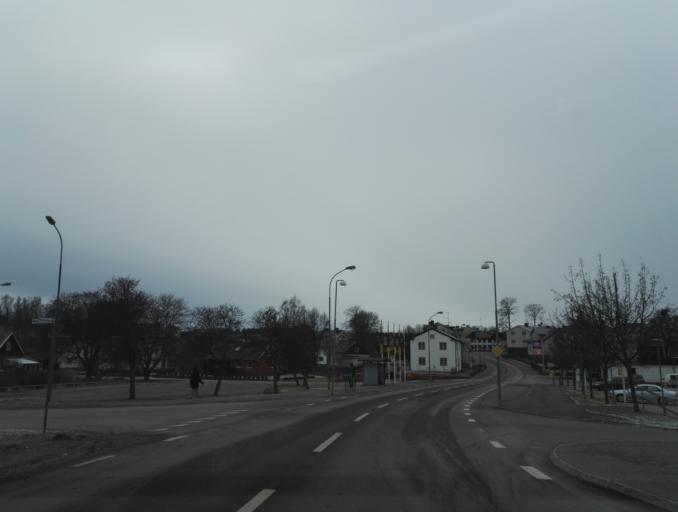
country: SE
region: Kalmar
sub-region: Hultsfreds Kommun
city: Virserum
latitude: 57.3219
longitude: 15.5825
